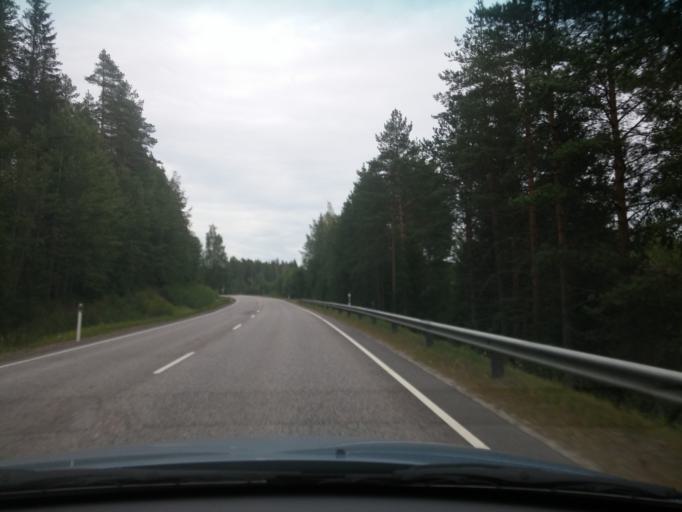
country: FI
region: Haeme
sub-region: Riihimaeki
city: Loppi
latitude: 60.7262
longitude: 24.4085
